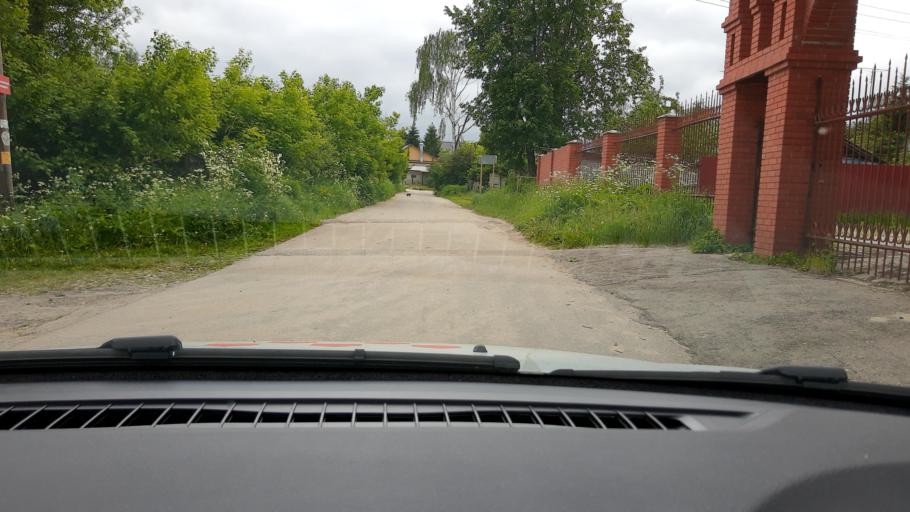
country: RU
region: Nizjnij Novgorod
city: Sitniki
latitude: 56.5194
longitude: 44.1166
